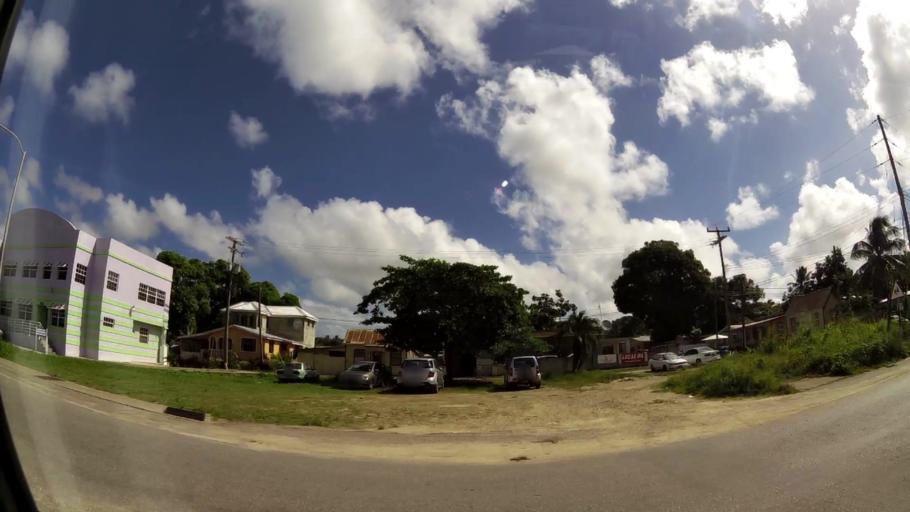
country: BB
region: Saint Peter
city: Speightstown
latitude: 13.2480
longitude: -59.6413
